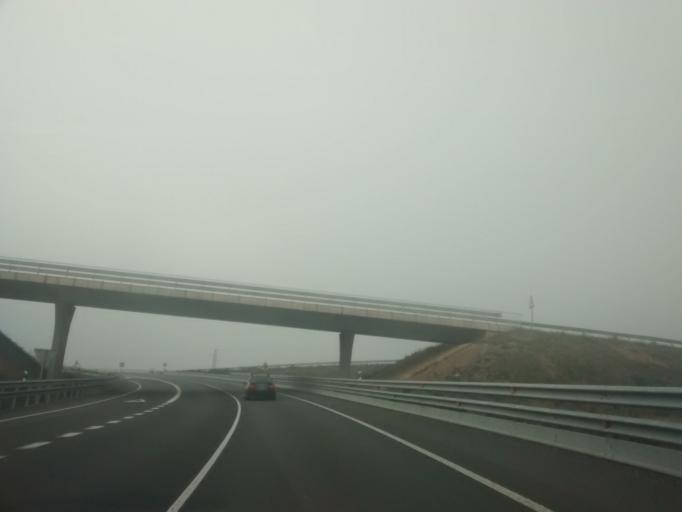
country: ES
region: La Rioja
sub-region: Provincia de La Rioja
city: Agoncillo
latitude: 42.4492
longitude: -2.3170
